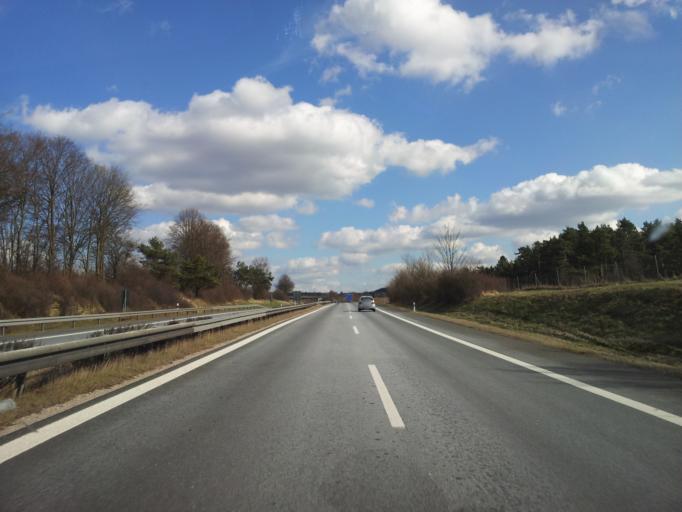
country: DE
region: Bavaria
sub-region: Upper Franconia
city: Kasendorf
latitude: 50.0104
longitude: 11.3279
